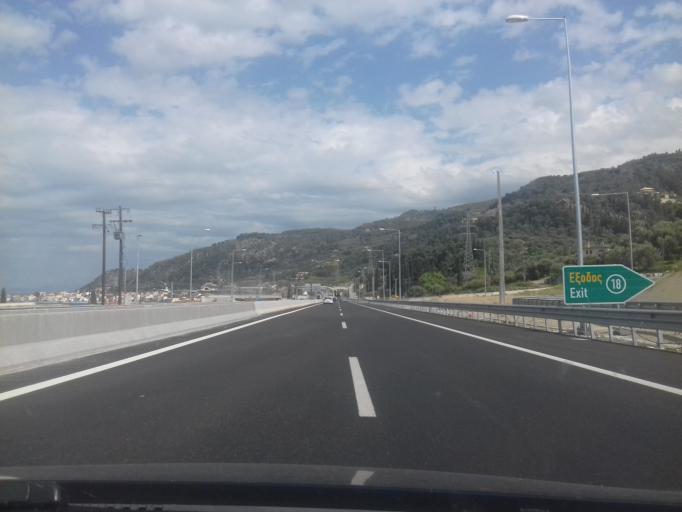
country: GR
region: West Greece
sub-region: Nomos Achaias
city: Aiyira
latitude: 38.1315
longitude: 22.4026
